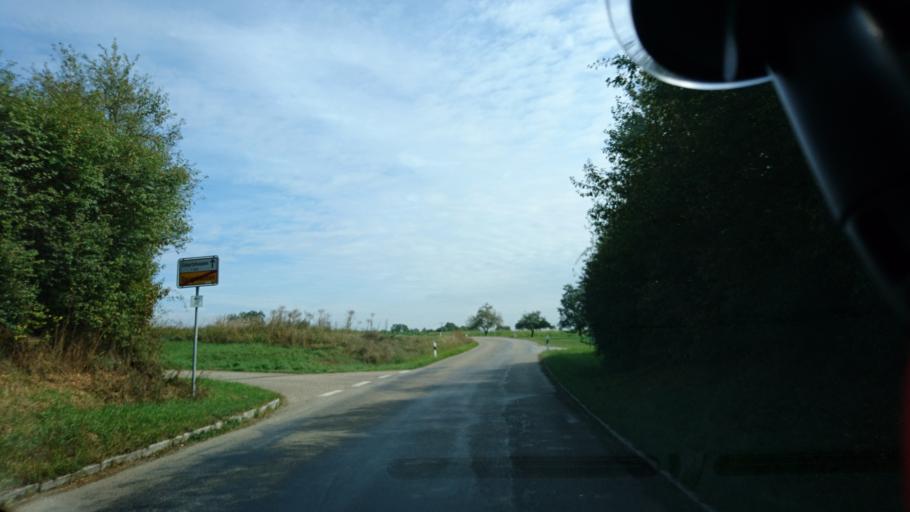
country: DE
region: Baden-Wuerttemberg
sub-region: Regierungsbezirk Stuttgart
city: Ilshofen
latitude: 49.1460
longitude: 9.9228
